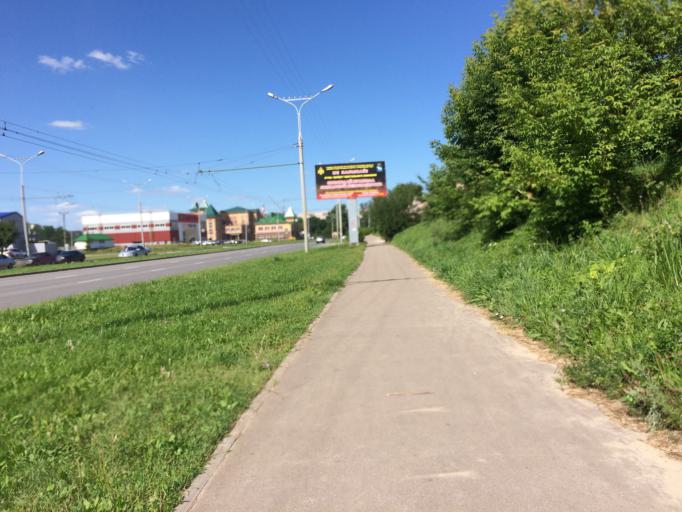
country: RU
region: Mariy-El
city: Yoshkar-Ola
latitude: 56.6264
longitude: 47.9358
